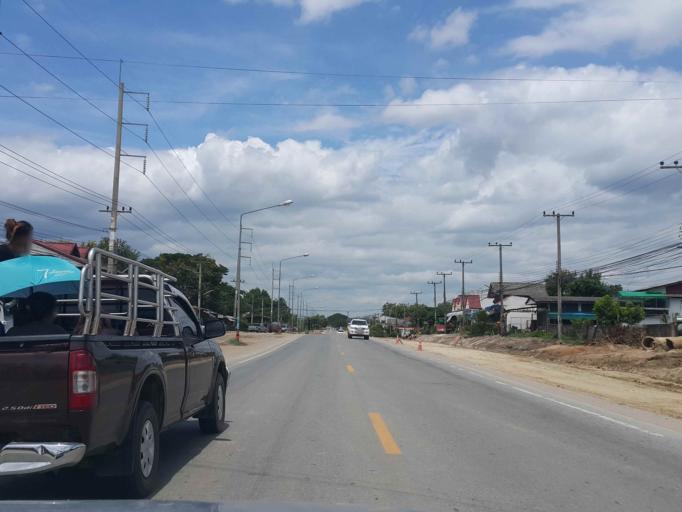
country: TH
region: Lamphun
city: Ban Hong
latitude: 18.3256
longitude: 98.8173
